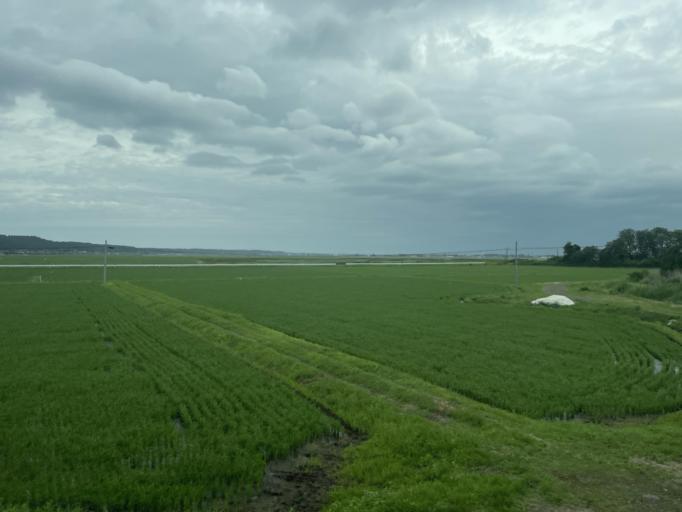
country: JP
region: Akita
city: Tenno
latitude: 39.9140
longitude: 139.9103
